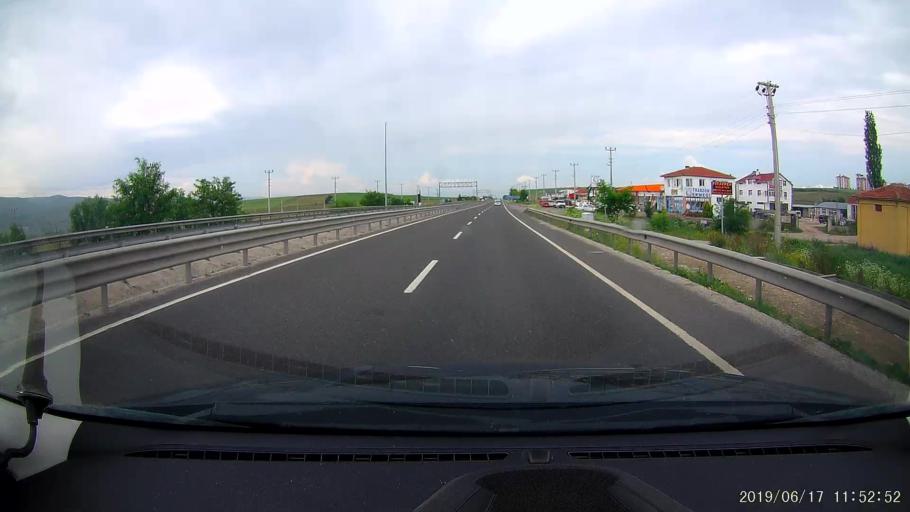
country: TR
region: Cankiri
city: Atkaracalar
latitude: 40.8070
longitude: 33.0741
